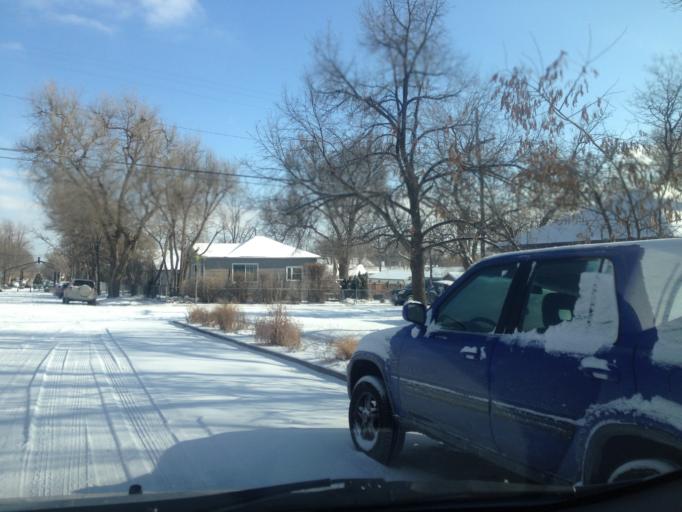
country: US
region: Colorado
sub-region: Boulder County
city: Lafayette
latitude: 39.9953
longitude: -105.0922
